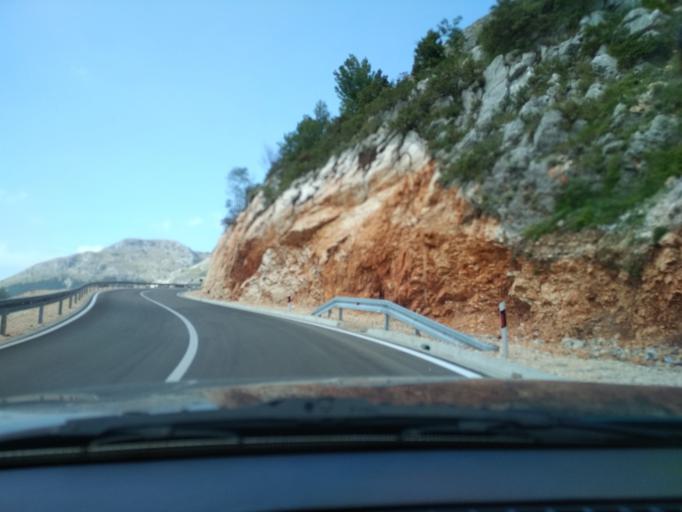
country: ME
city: Dobrota
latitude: 42.4385
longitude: 18.8387
